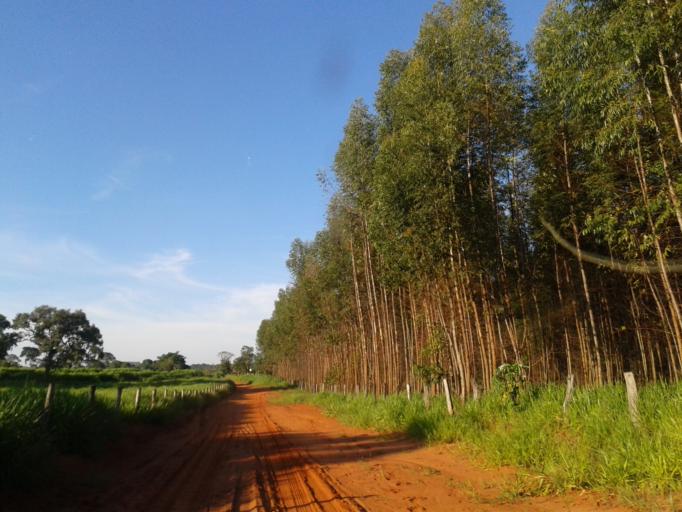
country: BR
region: Minas Gerais
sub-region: Santa Vitoria
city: Santa Vitoria
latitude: -18.9310
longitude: -49.8547
